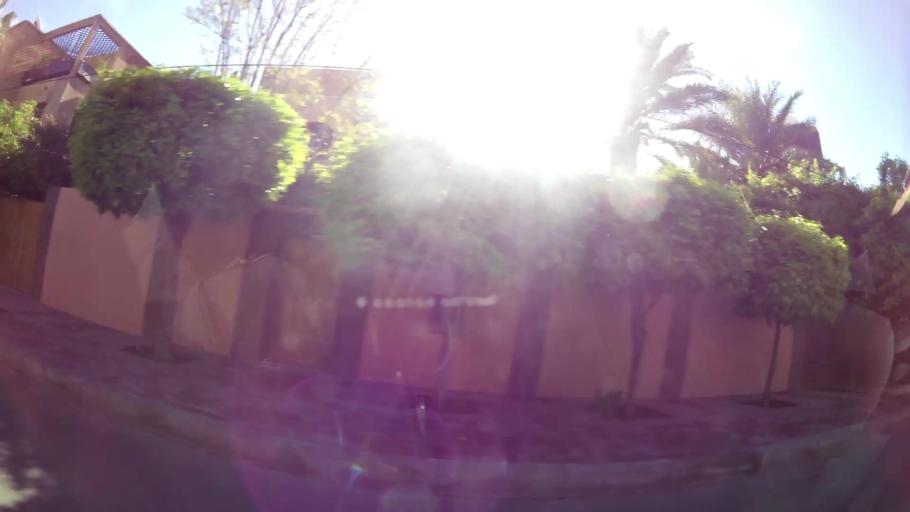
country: MA
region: Marrakech-Tensift-Al Haouz
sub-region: Marrakech
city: Marrakesh
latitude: 31.6452
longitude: -8.0159
